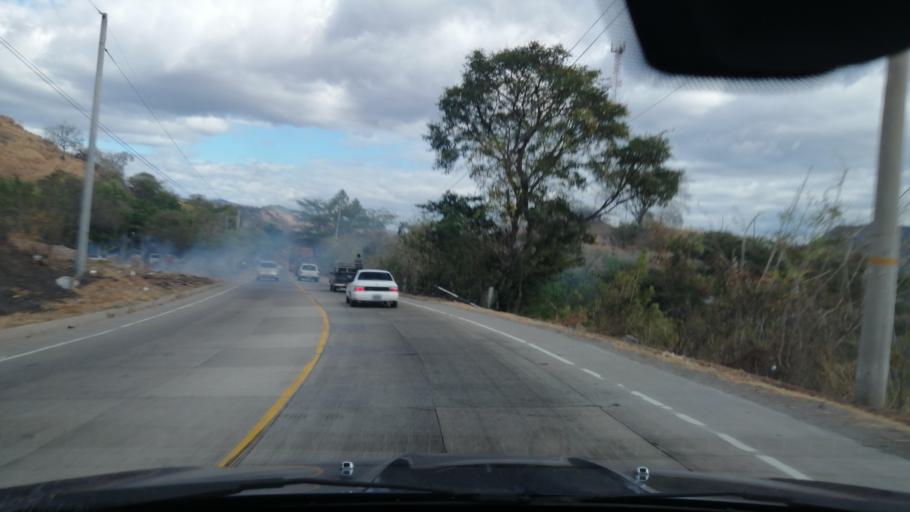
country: SV
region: Santa Ana
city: Texistepeque
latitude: 14.1381
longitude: -89.5122
